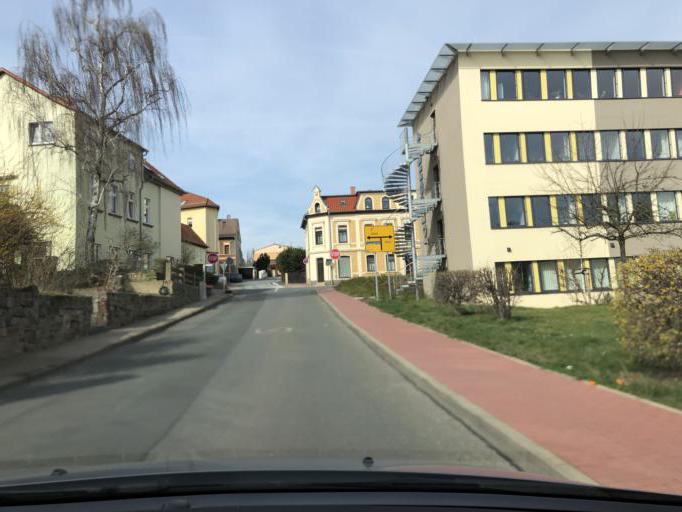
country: DE
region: Thuringia
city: Eisenberg
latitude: 50.9706
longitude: 11.9005
